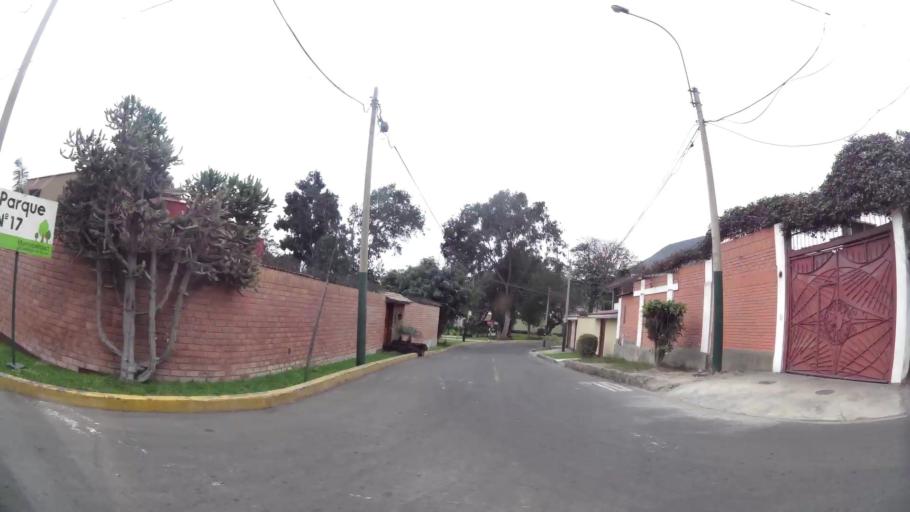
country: PE
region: Lima
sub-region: Lima
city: La Molina
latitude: -12.1082
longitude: -76.9604
